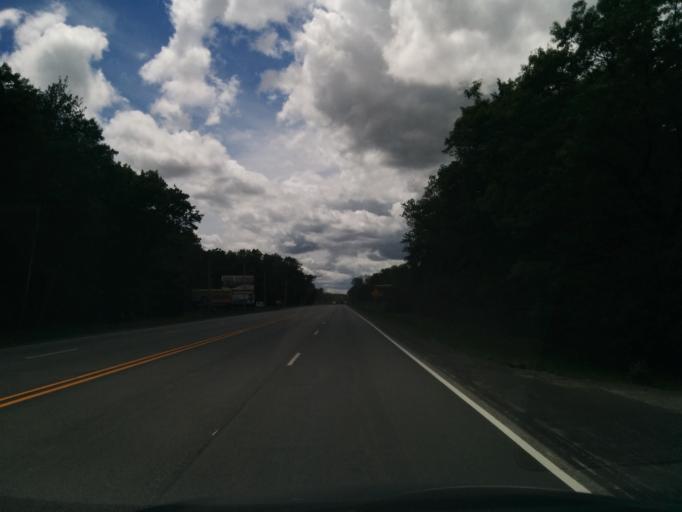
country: US
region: Indiana
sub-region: LaPorte County
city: Michigan City
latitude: 41.6755
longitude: -86.9670
